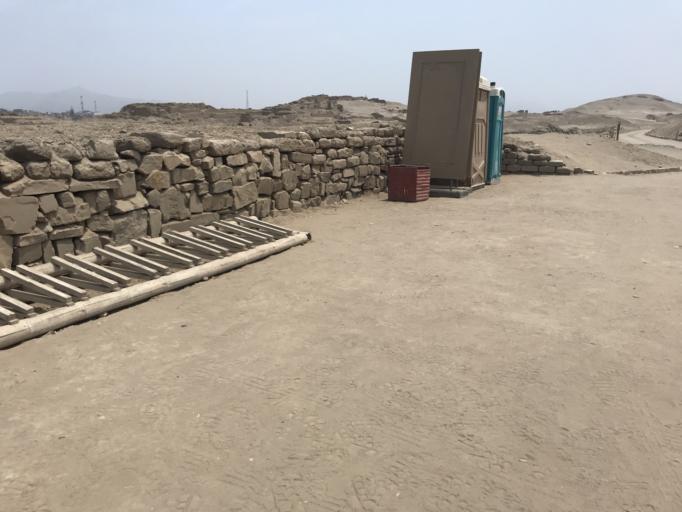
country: PE
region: Lima
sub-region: Lima
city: Punta Hermosa
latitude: -12.2594
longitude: -76.9006
